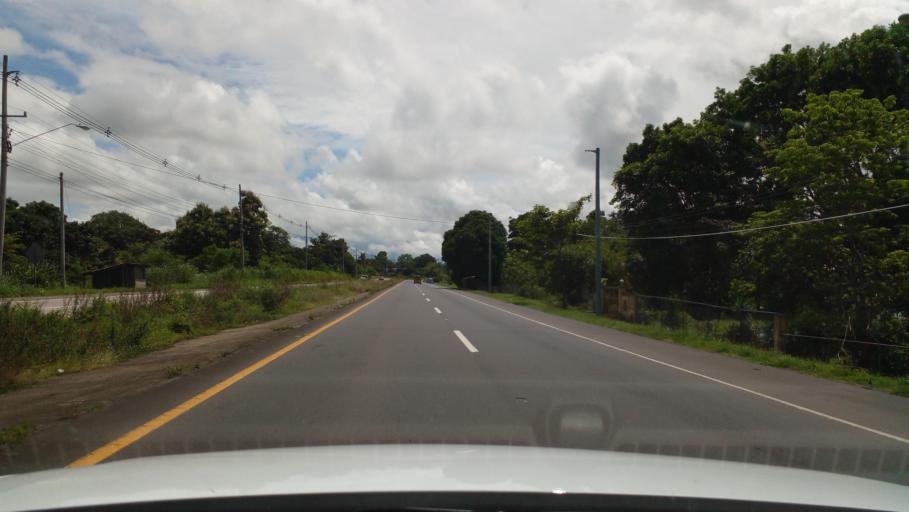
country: PA
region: Cocle
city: Rio Hato
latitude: 8.4093
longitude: -80.0782
